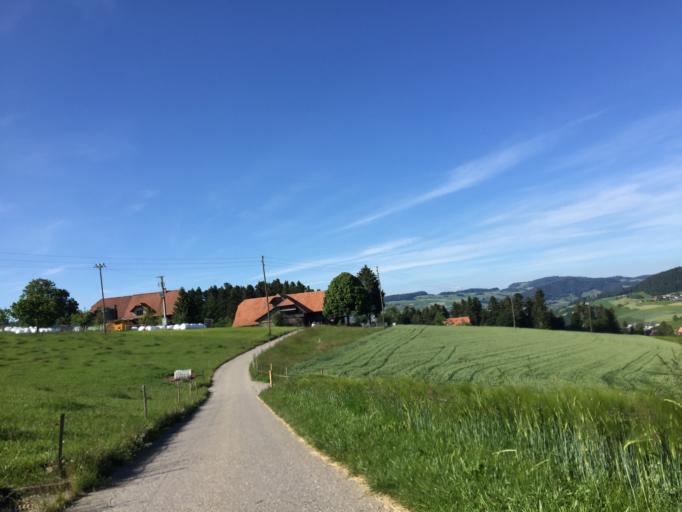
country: CH
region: Bern
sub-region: Bern-Mittelland District
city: Konolfingen
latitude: 46.8616
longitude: 7.6163
